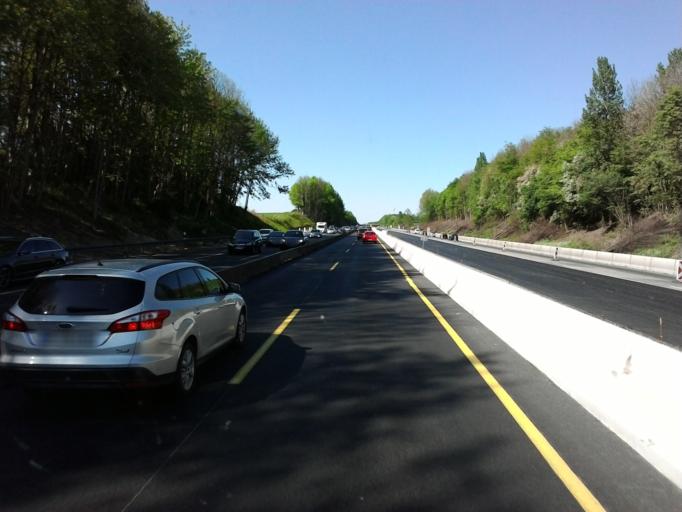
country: DE
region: North Rhine-Westphalia
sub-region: Regierungsbezirk Dusseldorf
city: Erkrath
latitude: 51.2496
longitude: 6.9125
